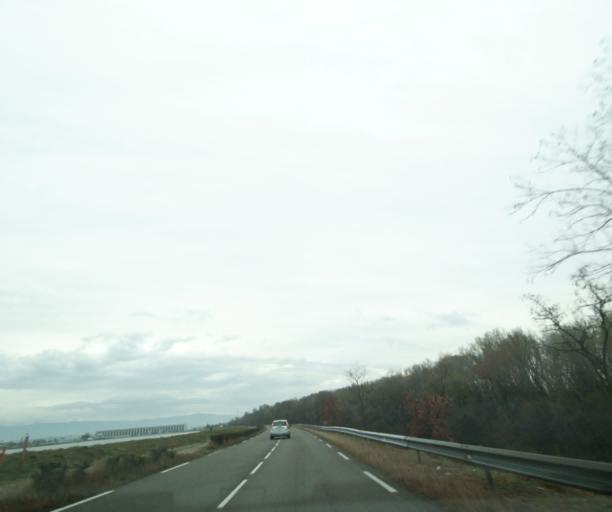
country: FR
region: Rhone-Alpes
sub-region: Departement de l'Ardeche
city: Cornas
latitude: 44.9670
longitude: 4.8621
